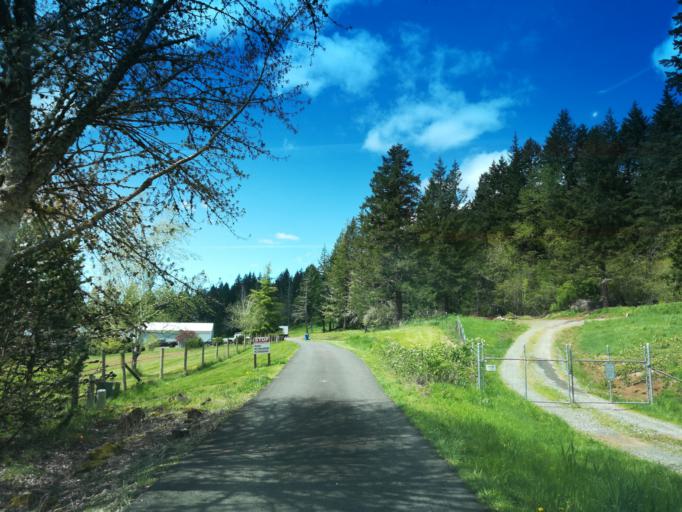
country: US
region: Oregon
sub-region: Clackamas County
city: Damascus
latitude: 45.4387
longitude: -122.4565
